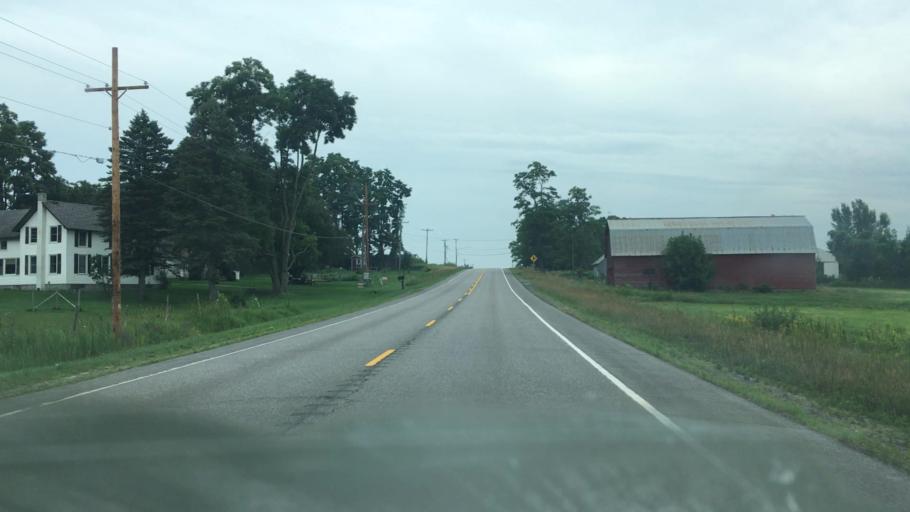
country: US
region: New York
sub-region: Clinton County
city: Morrisonville
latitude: 44.6455
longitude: -73.5671
